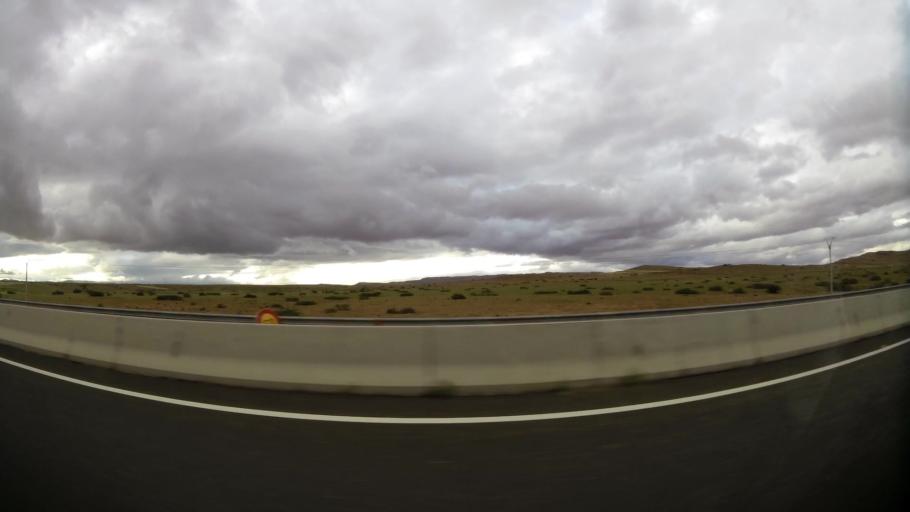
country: MA
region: Taza-Al Hoceima-Taounate
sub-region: Taza
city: Taza
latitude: 34.3075
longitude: -3.6964
